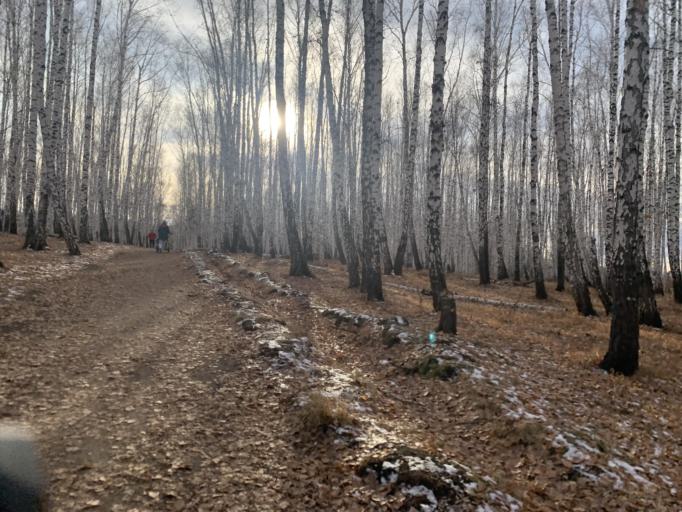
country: RU
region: Chelyabinsk
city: Roshchino
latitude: 55.2049
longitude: 61.3048
